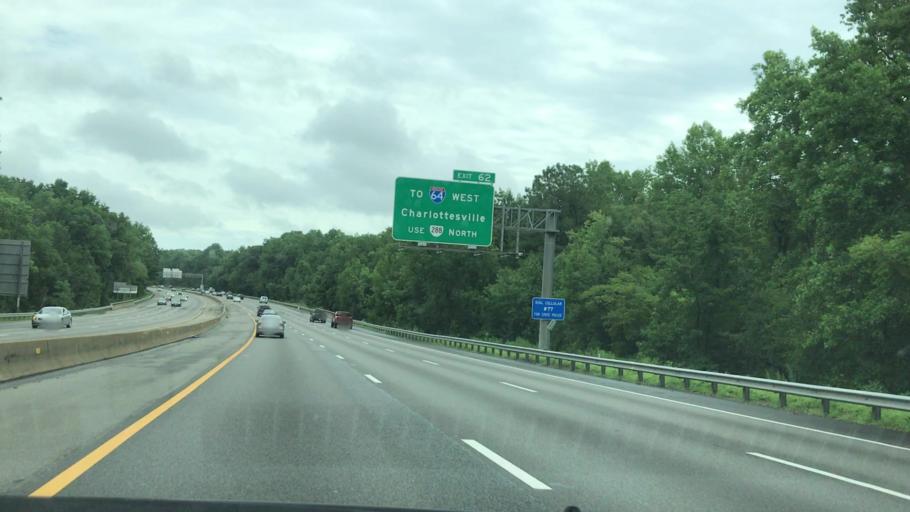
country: US
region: Virginia
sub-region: Chesterfield County
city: Chester
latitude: 37.3654
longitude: -77.4034
